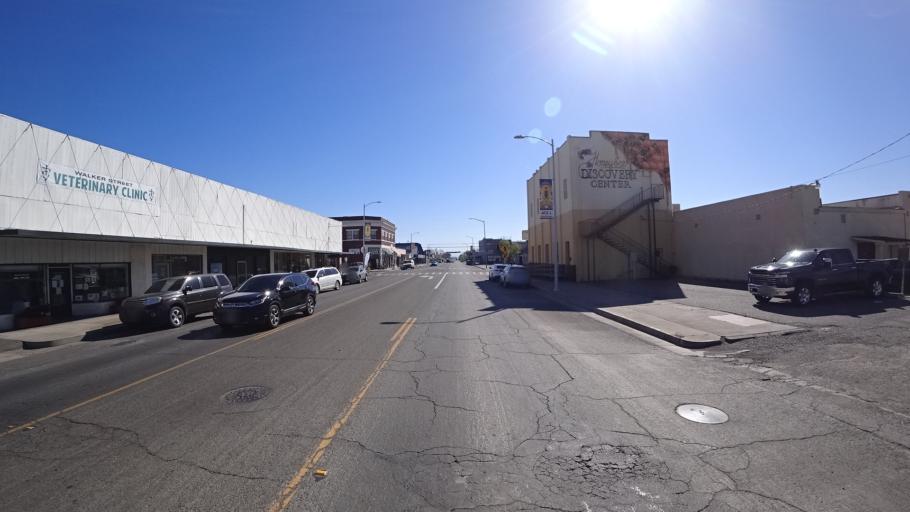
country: US
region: California
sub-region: Glenn County
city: Orland
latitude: 39.7474
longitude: -122.1961
